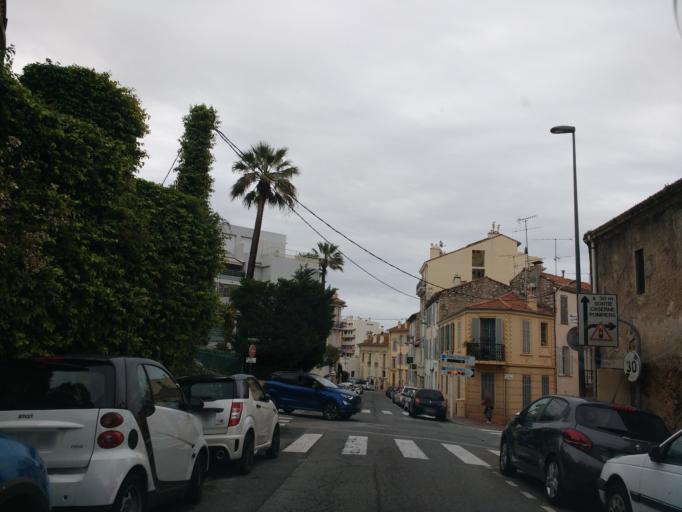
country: FR
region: Provence-Alpes-Cote d'Azur
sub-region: Departement des Alpes-Maritimes
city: Cannes
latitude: 43.5537
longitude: 7.0099
